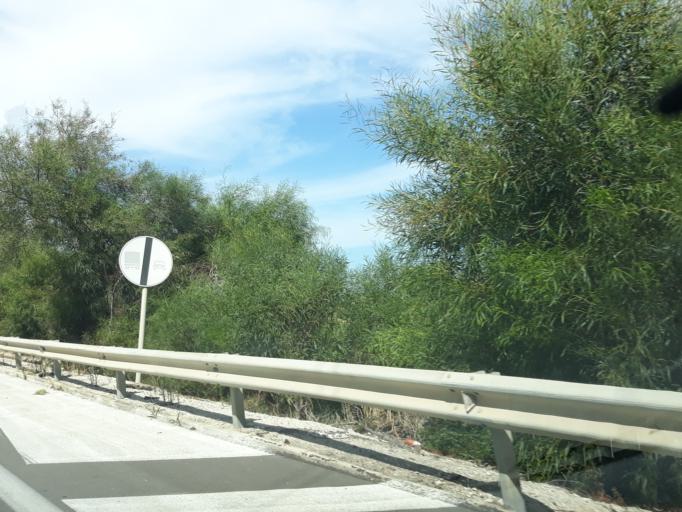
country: IT
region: Sicily
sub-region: Palermo
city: Termini Imerese
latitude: 37.9752
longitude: 13.6819
